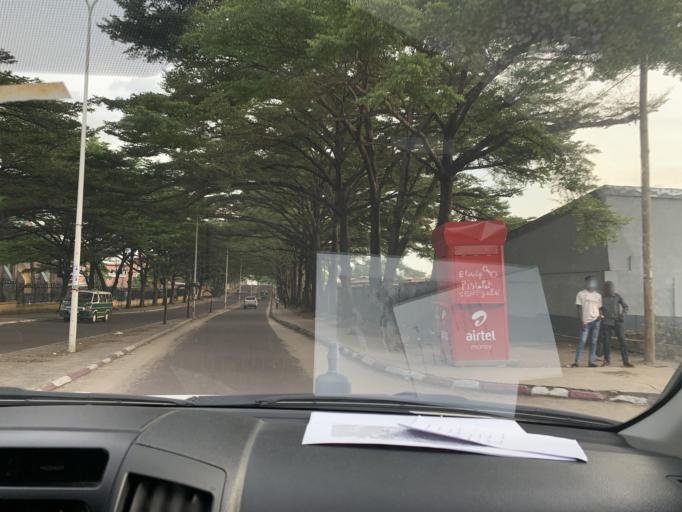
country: CG
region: Brazzaville
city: Brazzaville
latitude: -4.2677
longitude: 15.2840
